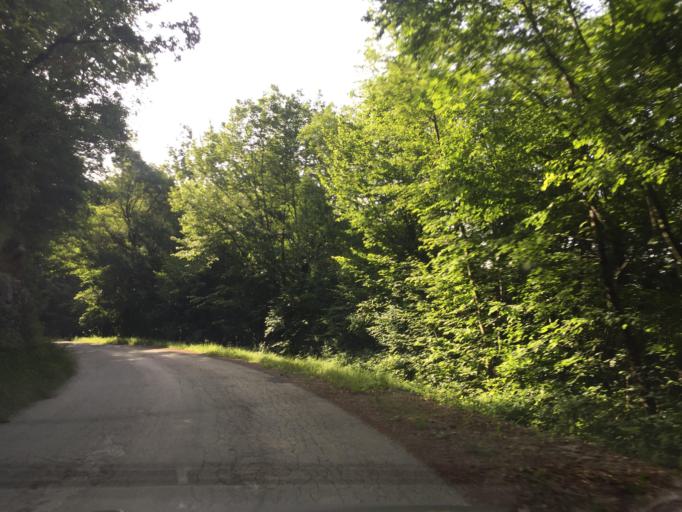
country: HR
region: Istarska
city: Buzet
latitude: 45.4709
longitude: 14.1075
